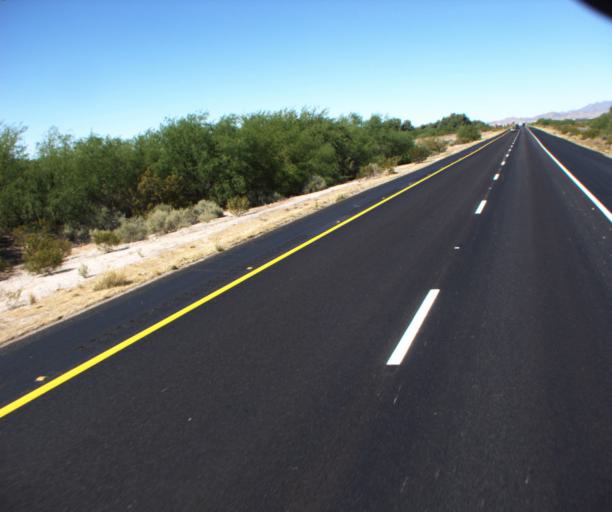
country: US
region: Arizona
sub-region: Maricopa County
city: Buckeye
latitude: 33.3201
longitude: -112.6229
